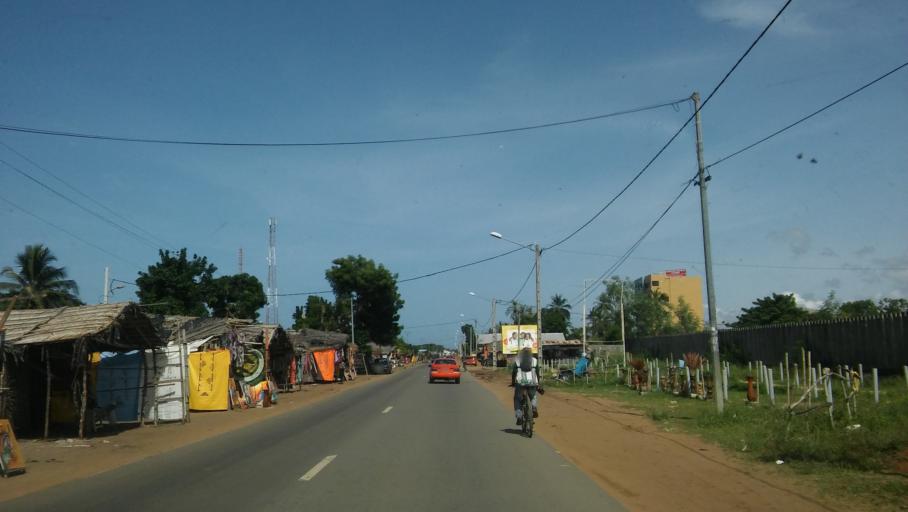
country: CI
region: Sud-Comoe
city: Grand-Bassam
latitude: 5.2103
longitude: -3.7573
